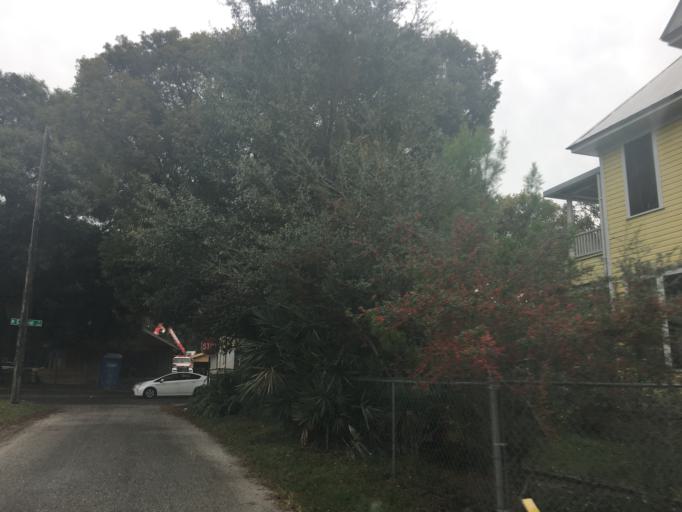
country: US
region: Florida
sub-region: Hillsborough County
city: Tampa
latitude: 27.9687
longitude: -82.4557
